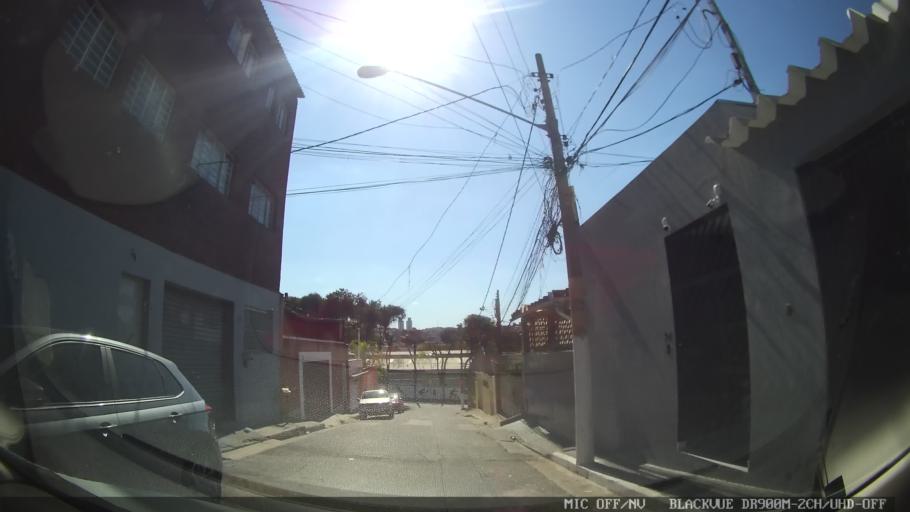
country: BR
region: Sao Paulo
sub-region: Sao Paulo
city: Sao Paulo
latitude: -23.4928
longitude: -46.6548
